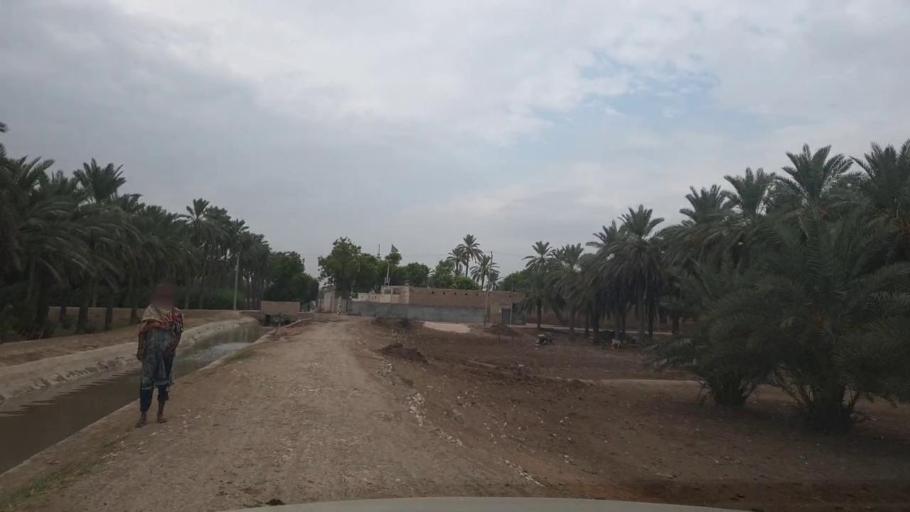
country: PK
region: Sindh
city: Sukkur
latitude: 27.6243
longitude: 68.8200
